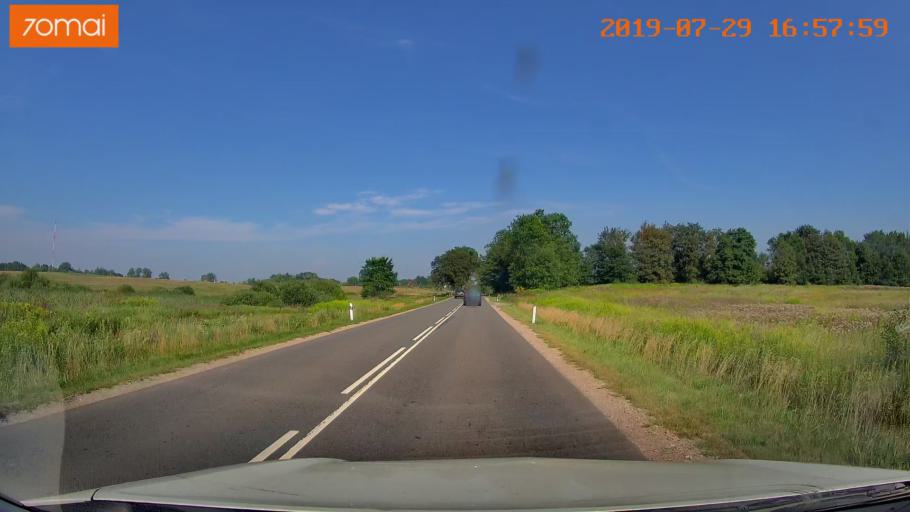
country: RU
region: Kaliningrad
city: Volochayevskoye
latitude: 54.8155
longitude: 20.1950
